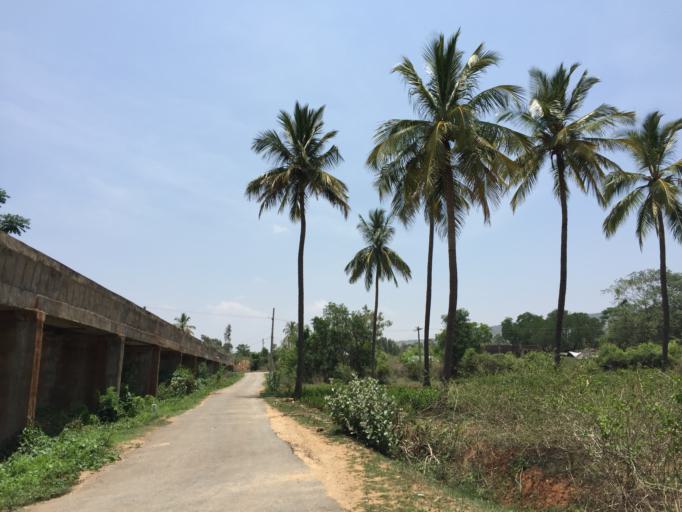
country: IN
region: Karnataka
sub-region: Mandya
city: Malavalli
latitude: 12.3848
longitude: 77.2244
